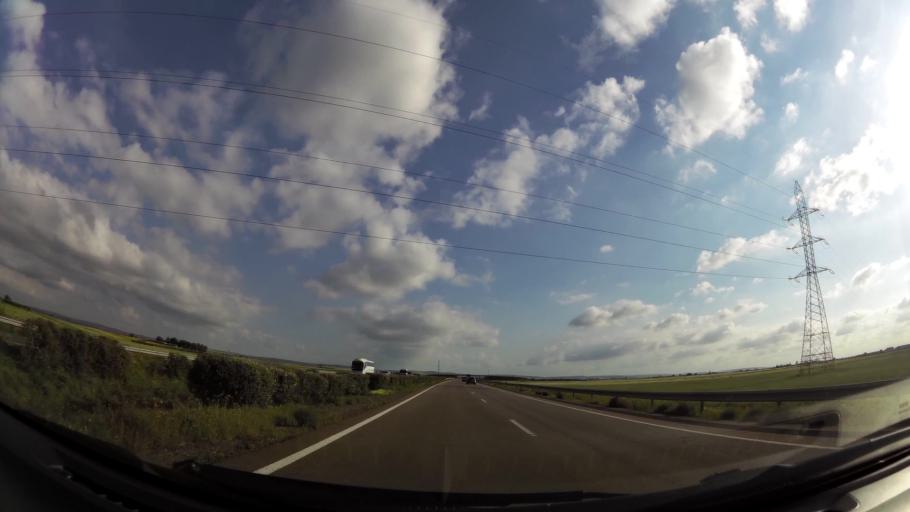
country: MA
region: Chaouia-Ouardigha
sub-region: Settat Province
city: Berrechid
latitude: 33.1543
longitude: -7.5715
